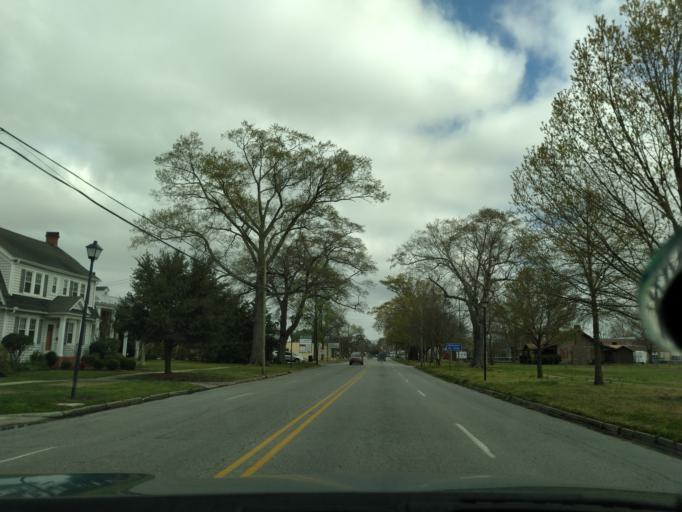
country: US
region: North Carolina
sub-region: Chowan County
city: Edenton
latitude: 36.0664
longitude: -76.6065
